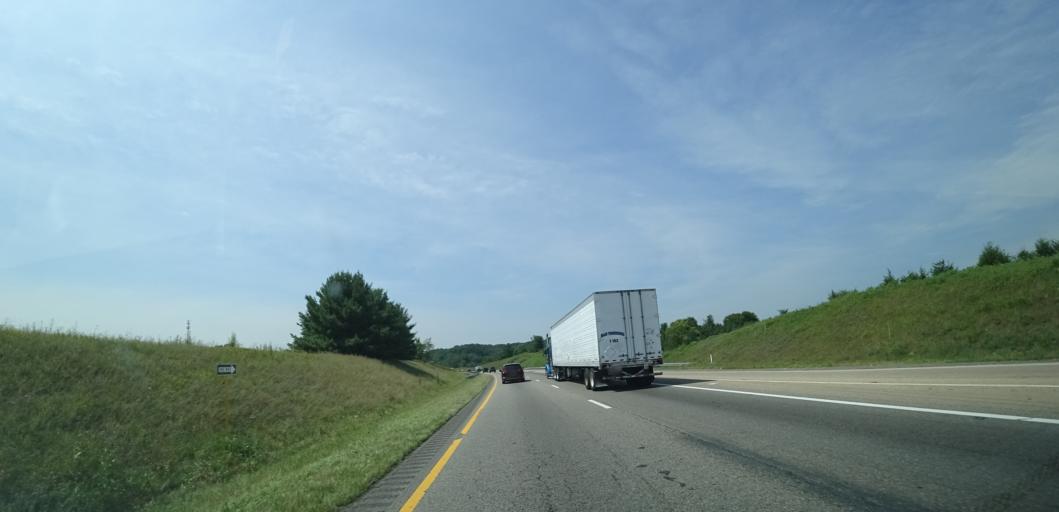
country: US
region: Virginia
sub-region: Augusta County
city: Verona
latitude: 38.1643
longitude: -79.0128
